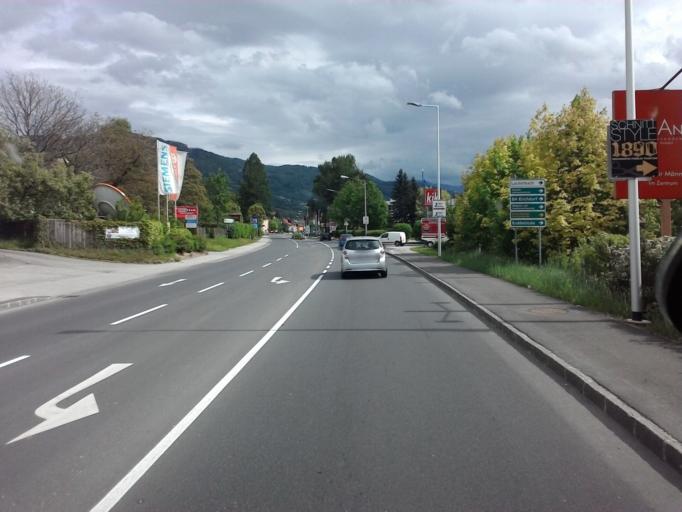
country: AT
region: Upper Austria
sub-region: Politischer Bezirk Kirchdorf an der Krems
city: Micheldorf in Oberoesterreich
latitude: 47.9050
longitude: 14.1206
